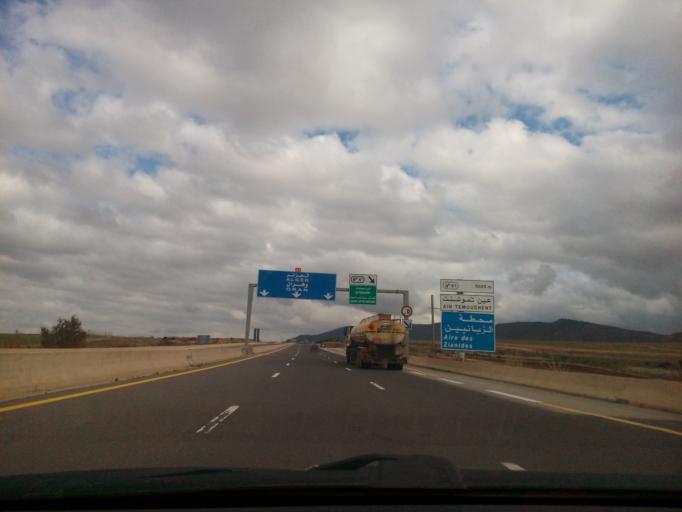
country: DZ
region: Tlemcen
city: Bensekrane
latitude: 34.9882
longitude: -1.2164
